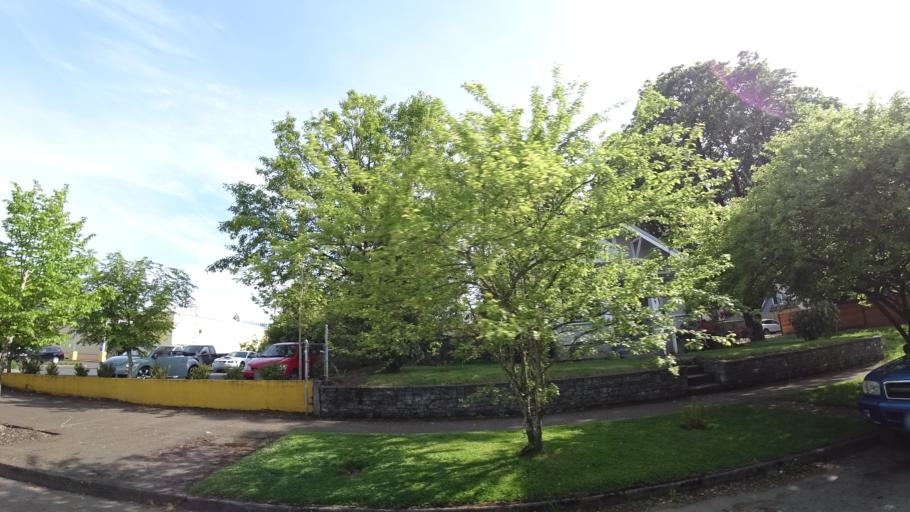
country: US
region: Oregon
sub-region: Multnomah County
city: Lents
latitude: 45.4784
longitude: -122.6099
